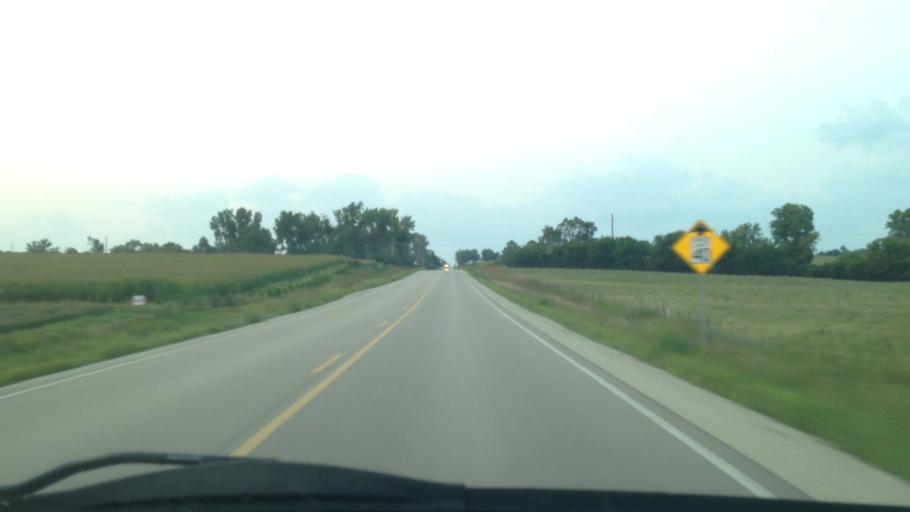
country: US
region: Iowa
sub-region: Benton County
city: Urbana
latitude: 42.2159
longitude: -91.8714
